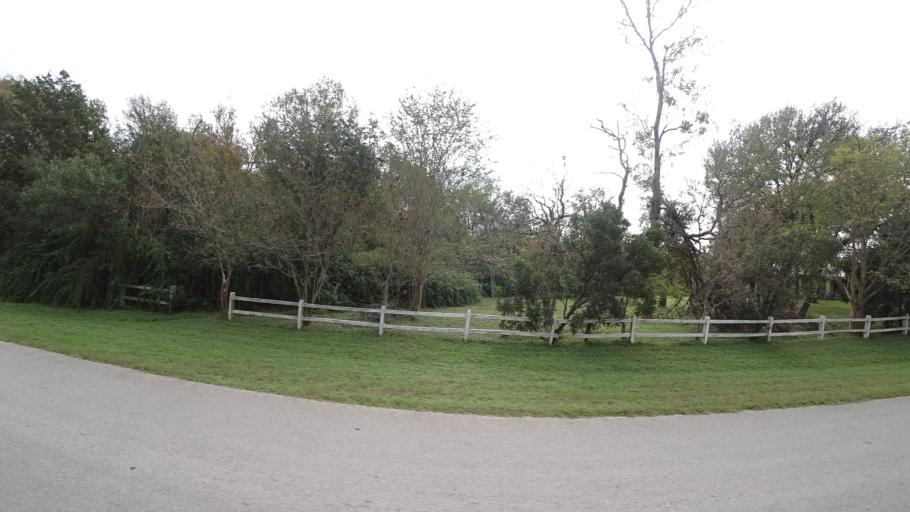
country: US
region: Texas
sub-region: Travis County
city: Shady Hollow
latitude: 30.1373
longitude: -97.8841
